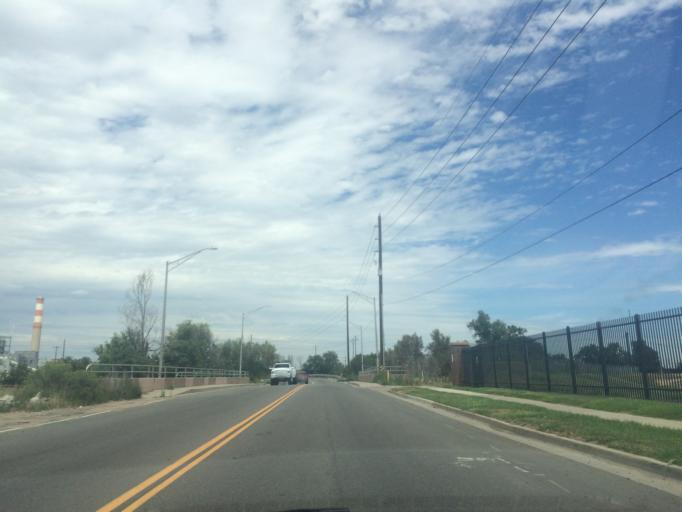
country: US
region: Colorado
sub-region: Adams County
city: Commerce City
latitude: 39.8000
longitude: -104.9594
